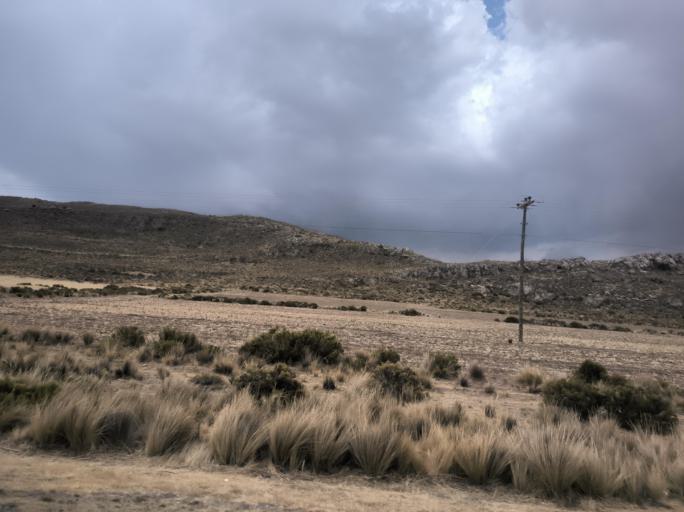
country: BO
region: Oruro
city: Challapata
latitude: -18.7659
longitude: -66.8587
